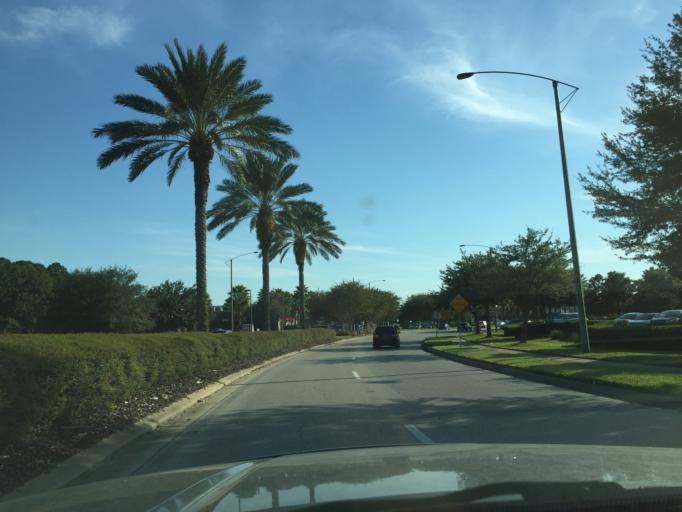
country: US
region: Florida
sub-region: Orange County
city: Oak Ridge
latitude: 28.4917
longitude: -81.4283
